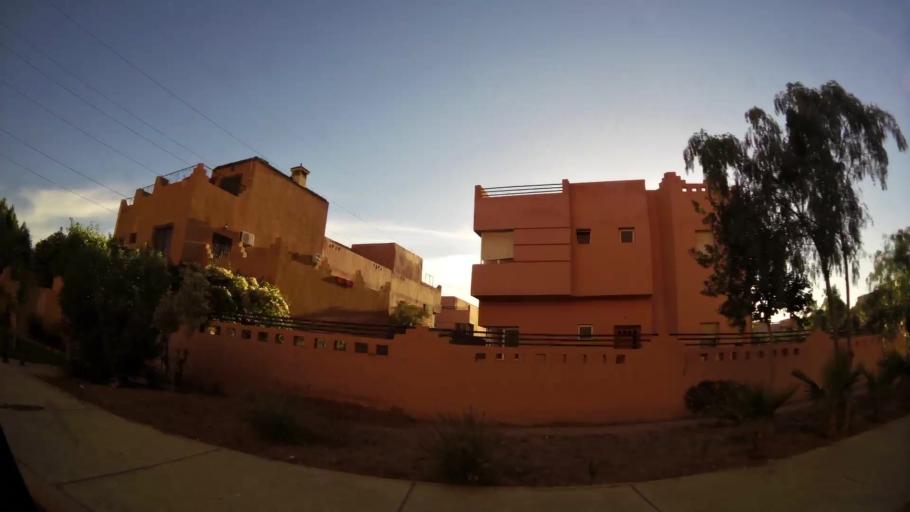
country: MA
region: Marrakech-Tensift-Al Haouz
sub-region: Marrakech
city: Marrakesh
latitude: 31.7432
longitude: -8.1120
